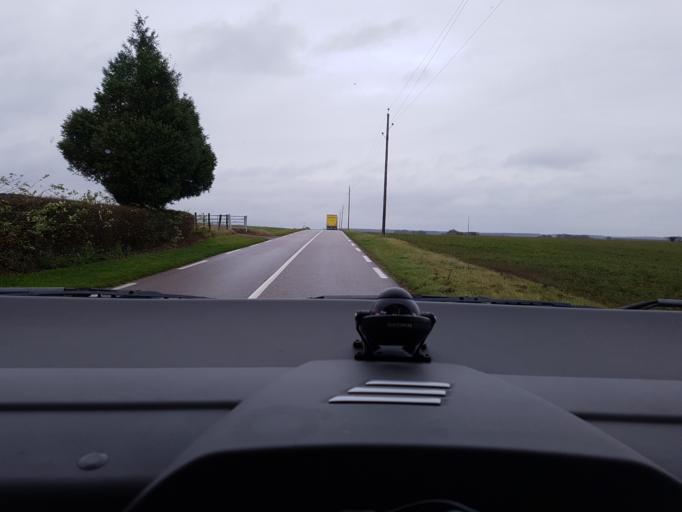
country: FR
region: Haute-Normandie
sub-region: Departement de l'Eure
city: Etrepagny
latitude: 49.3861
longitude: 1.5940
